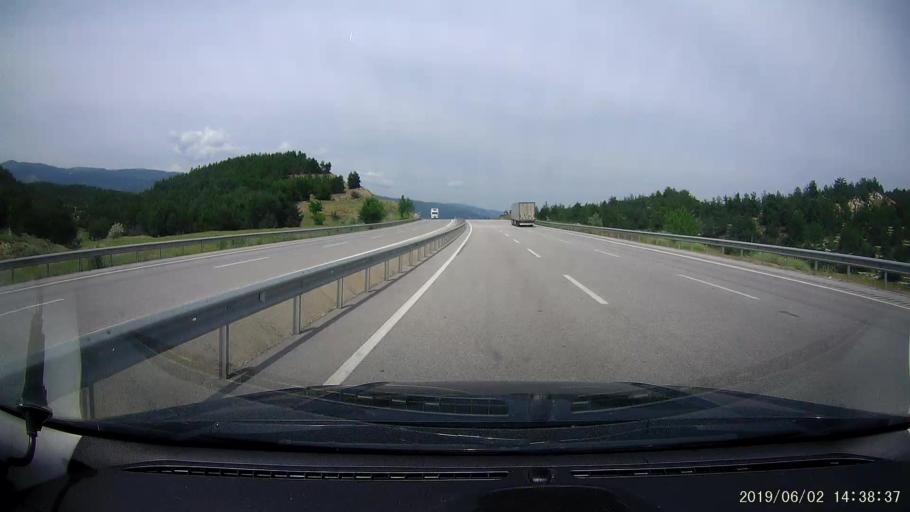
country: TR
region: Corum
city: Hacihamza
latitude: 41.0576
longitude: 34.2847
